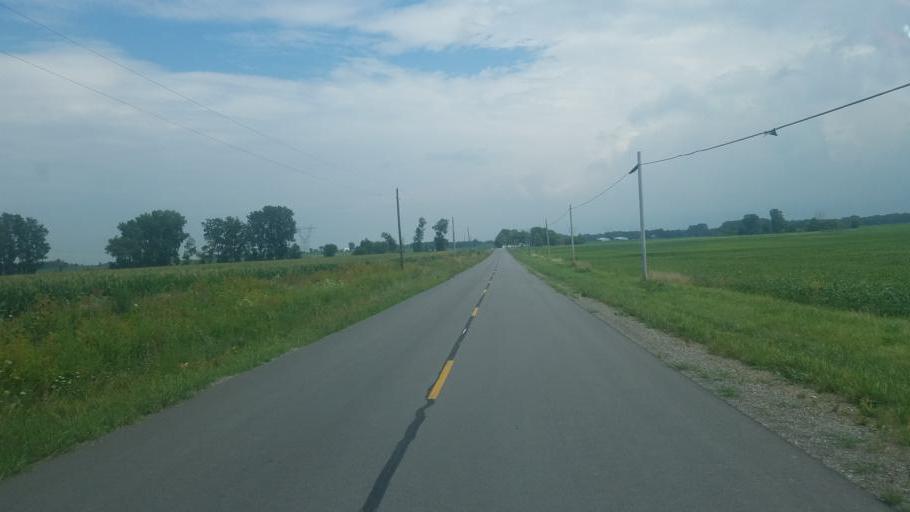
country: US
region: Ohio
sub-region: Logan County
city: Northwood
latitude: 40.3918
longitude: -83.5962
